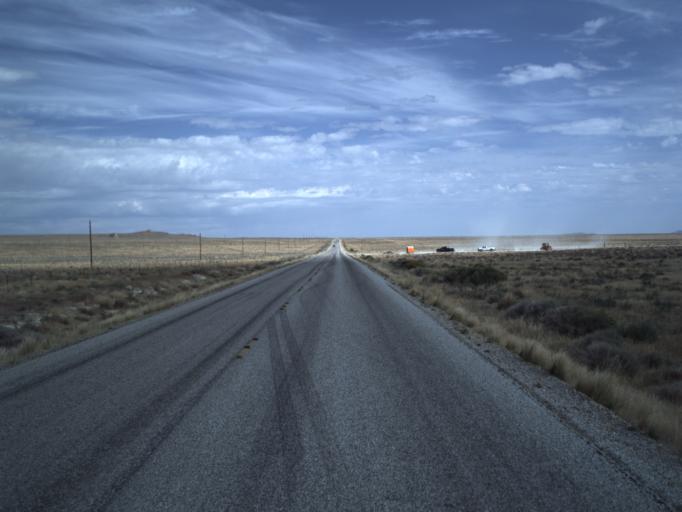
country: US
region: Utah
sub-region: Tooele County
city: Wendover
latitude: 41.4638
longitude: -113.6483
